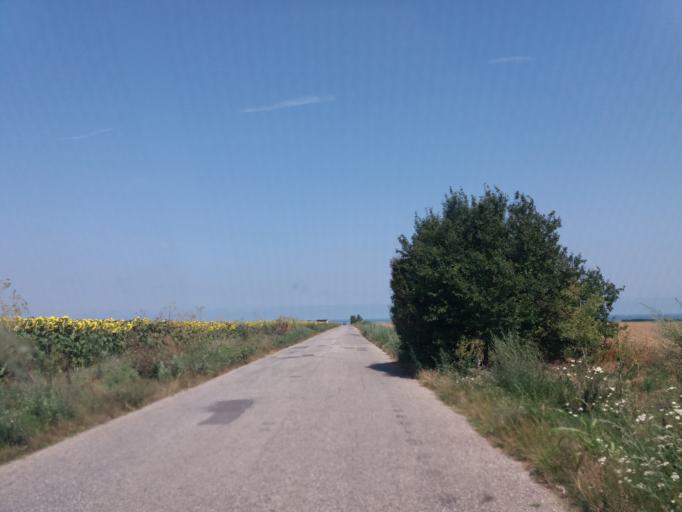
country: RO
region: Constanta
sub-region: Comuna Corbu
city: Corbu
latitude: 44.4245
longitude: 28.6919
